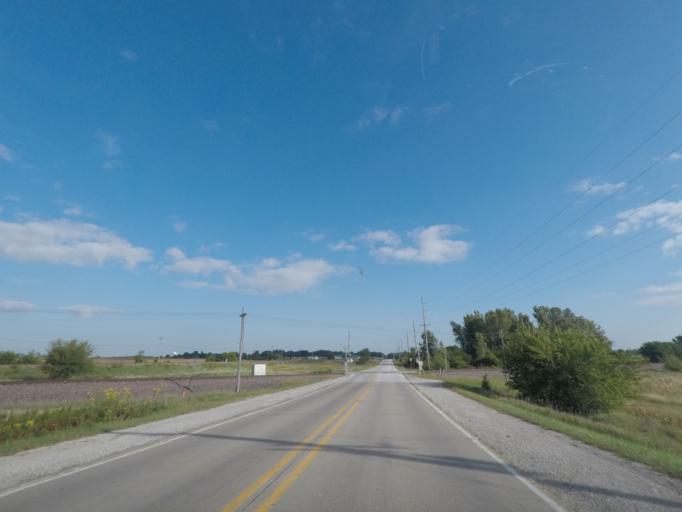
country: US
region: Iowa
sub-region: Story County
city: Nevada
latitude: 42.0075
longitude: -93.4629
